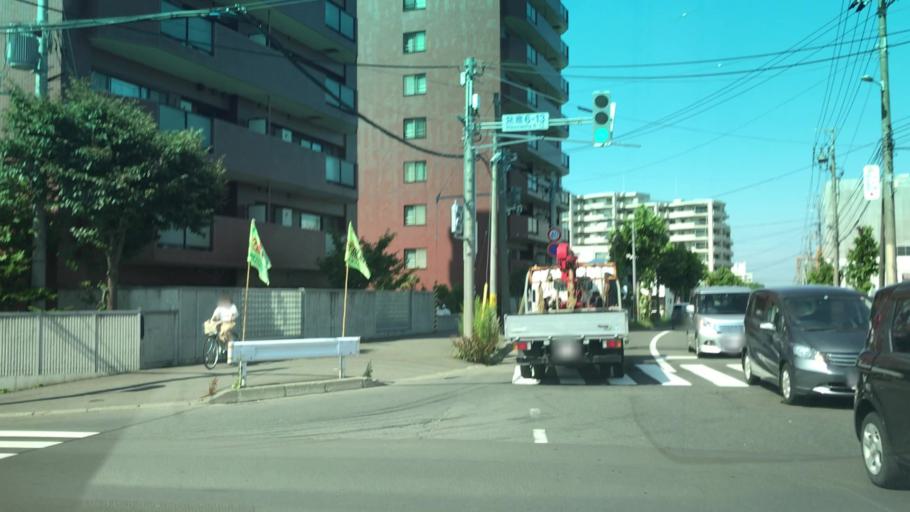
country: JP
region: Hokkaido
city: Sapporo
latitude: 43.0933
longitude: 141.2716
